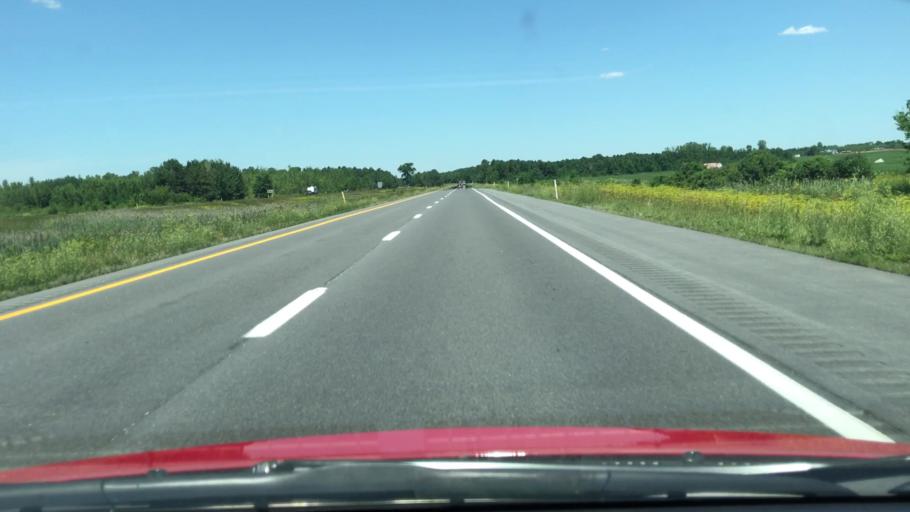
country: US
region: New York
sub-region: Clinton County
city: Cumberland Head
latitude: 44.8326
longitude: -73.4464
